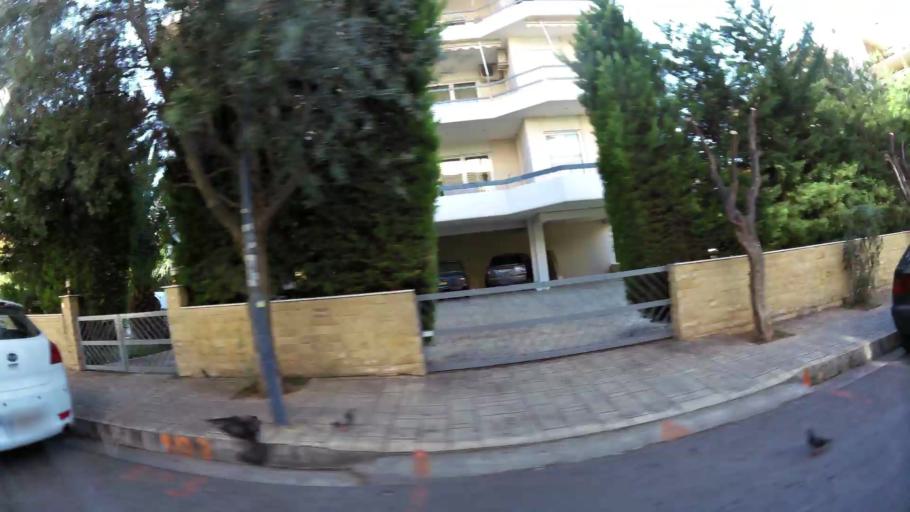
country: GR
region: Attica
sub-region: Nomarchia Athinas
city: Vrilissia
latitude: 38.0352
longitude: 23.8320
